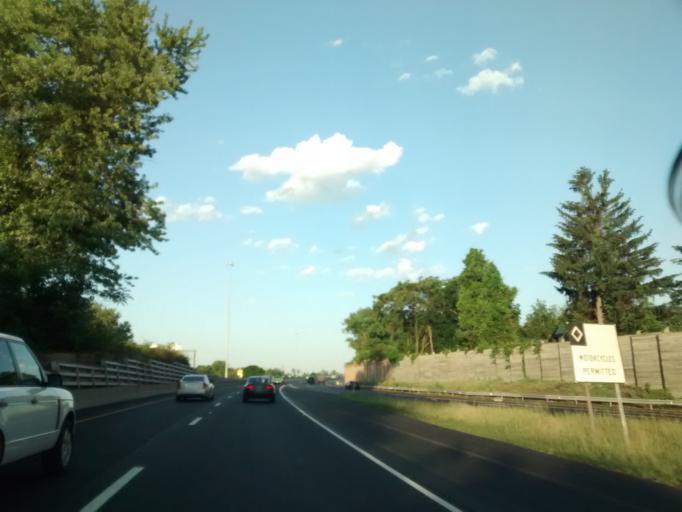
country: US
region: Connecticut
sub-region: Hartford County
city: Hartford
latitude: 41.7653
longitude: -72.6509
